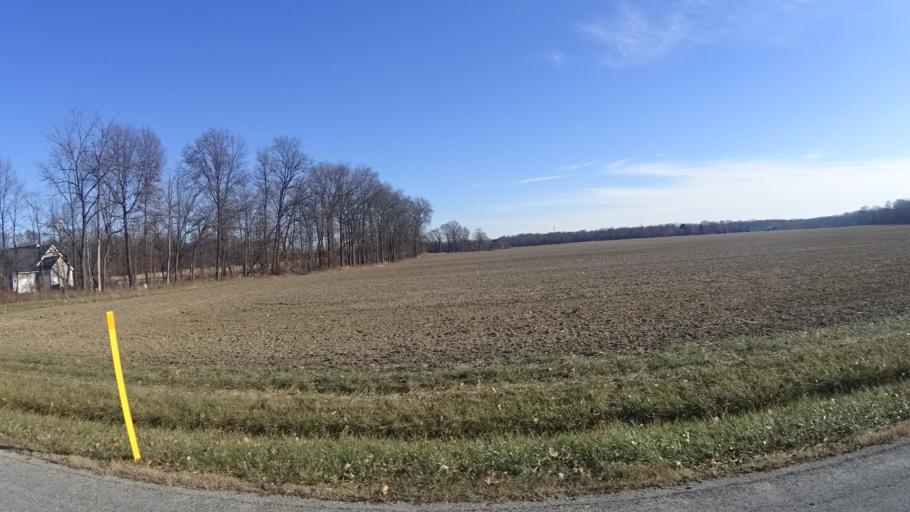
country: US
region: Ohio
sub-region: Lorain County
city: Vermilion-on-the-Lake
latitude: 41.3665
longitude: -82.3286
